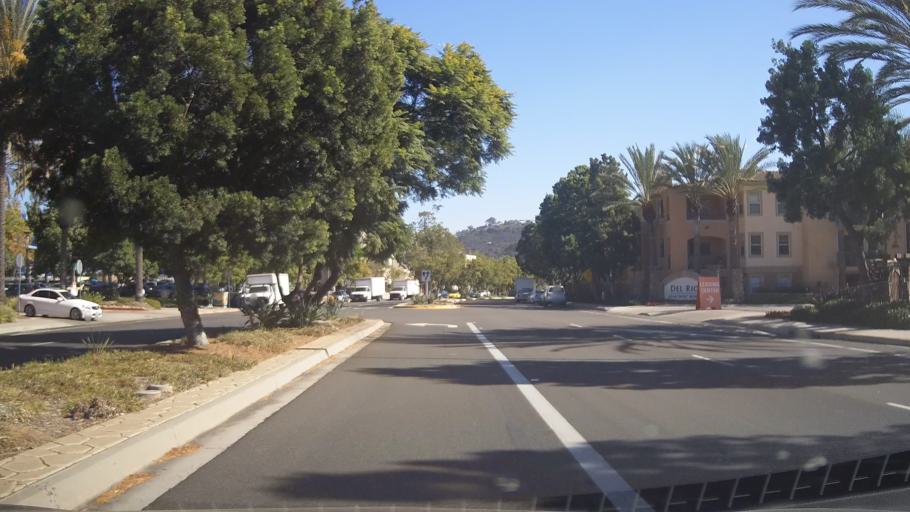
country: US
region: California
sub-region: San Diego County
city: San Diego
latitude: 32.7797
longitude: -117.1287
